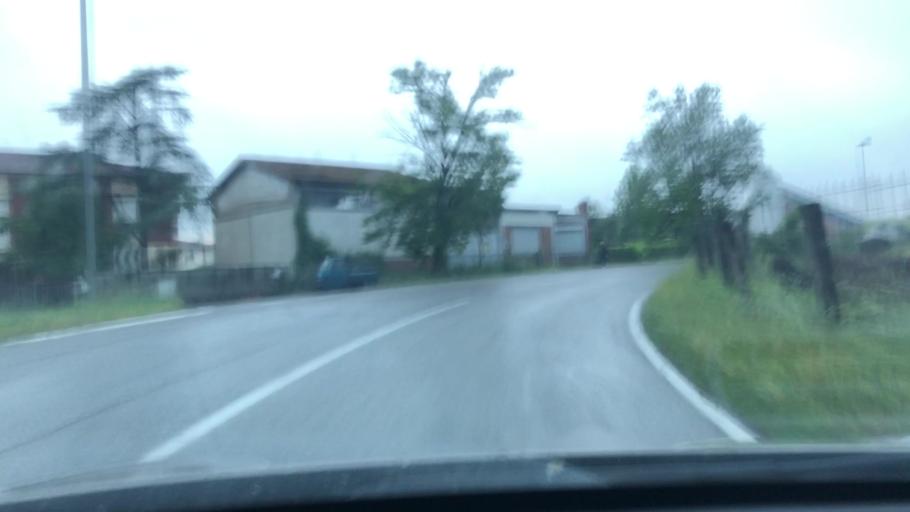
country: IT
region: Tuscany
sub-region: Province of Pisa
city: Il Romito
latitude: 43.6447
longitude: 10.6450
